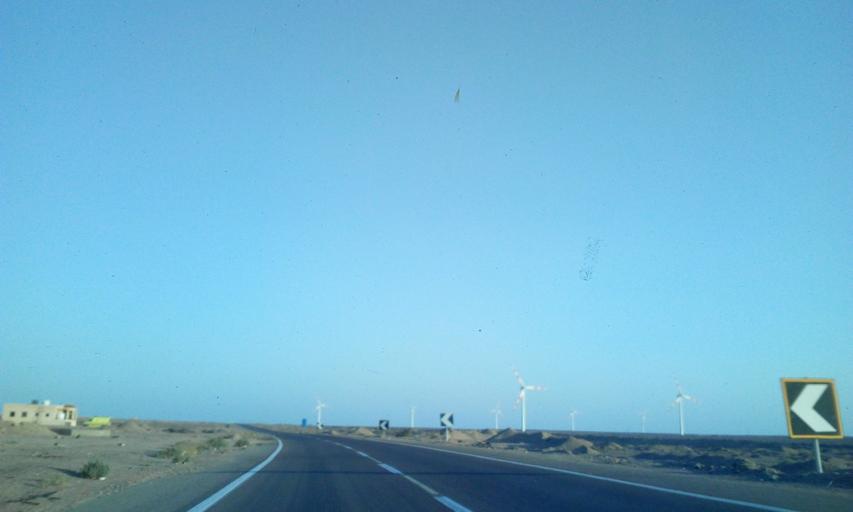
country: EG
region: South Sinai
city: Tor
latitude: 28.0770
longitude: 33.2564
